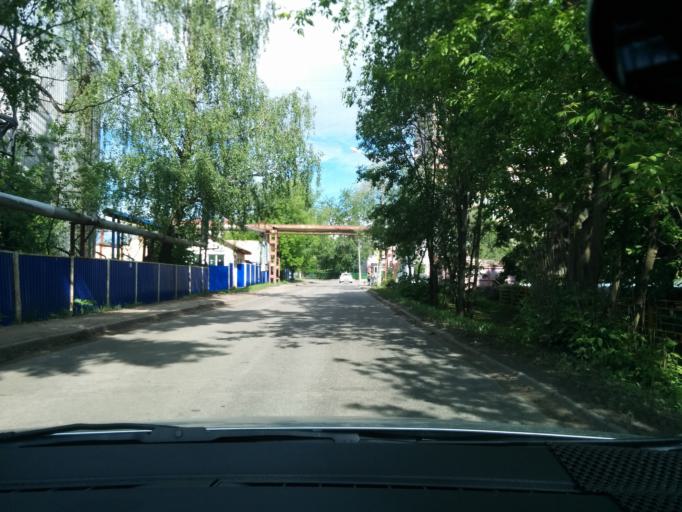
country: RU
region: Moskovskaya
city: Lobnya
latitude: 56.0158
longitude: 37.4721
